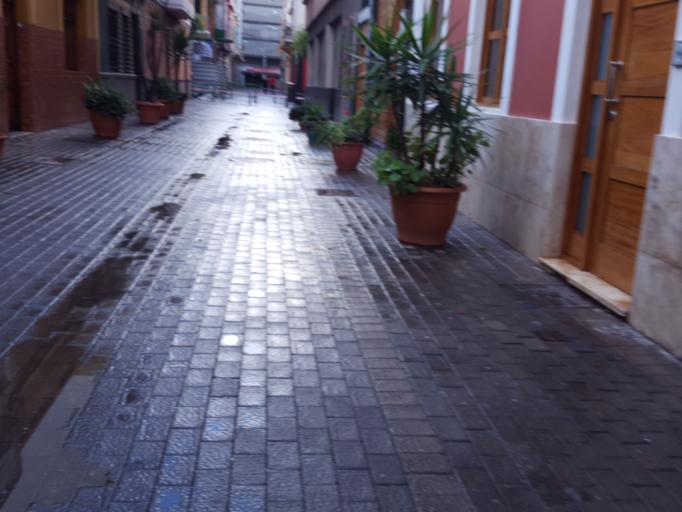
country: ES
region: Canary Islands
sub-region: Provincia de Las Palmas
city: Las Palmas de Gran Canaria
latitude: 28.1391
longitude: -15.4351
